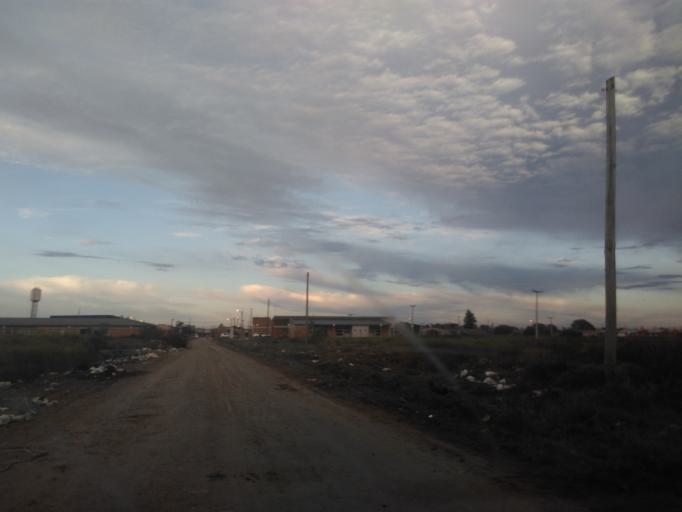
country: AR
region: Chaco
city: Fontana
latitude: -27.4543
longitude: -59.0432
